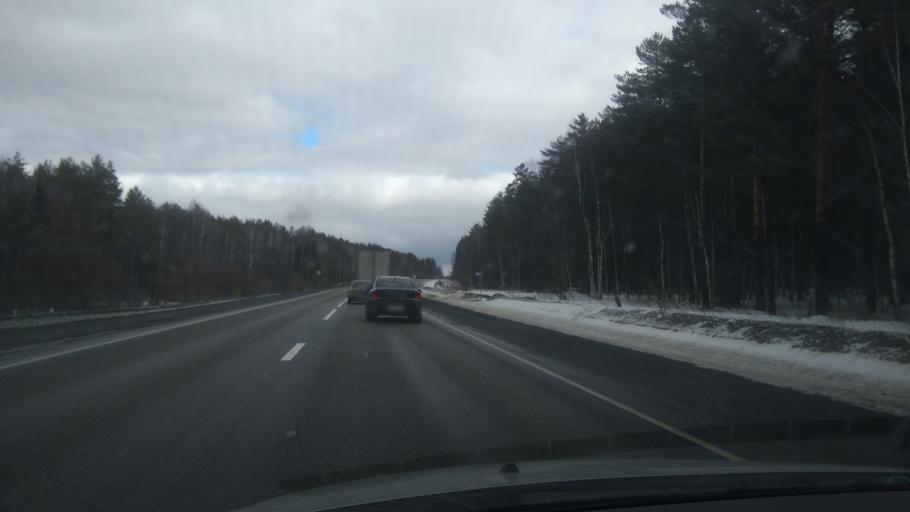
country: RU
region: Sverdlovsk
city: Bisert'
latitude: 56.8303
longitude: 58.7781
